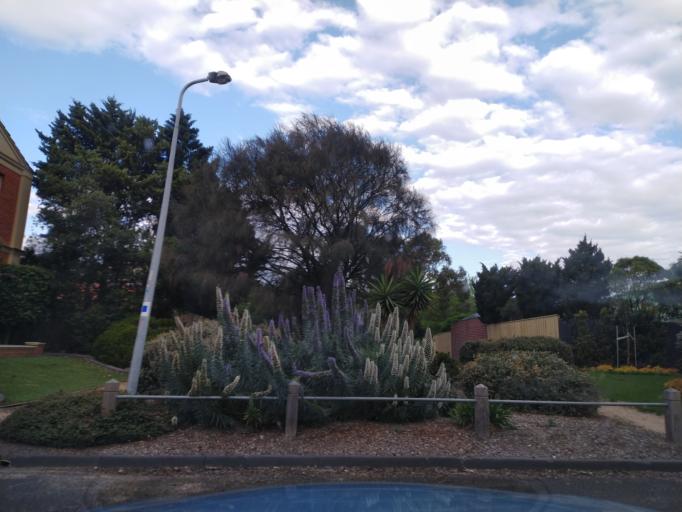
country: AU
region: Victoria
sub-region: Hobsons Bay
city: Williamstown North
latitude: -37.8573
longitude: 144.8778
